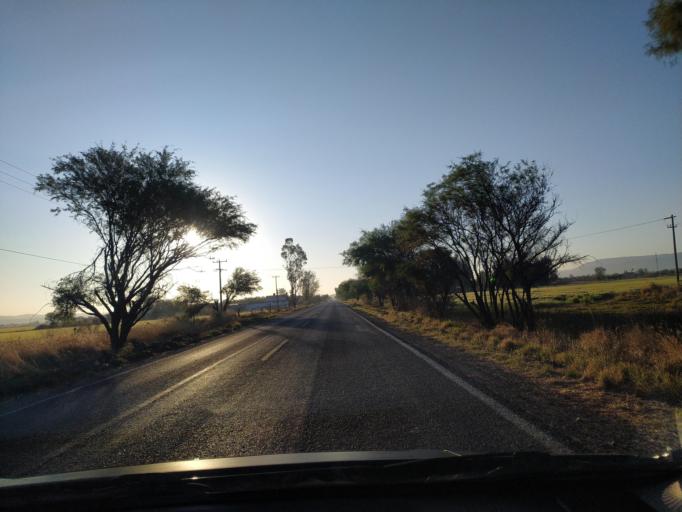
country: MX
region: Guanajuato
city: Ciudad Manuel Doblado
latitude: 20.7431
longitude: -101.8913
